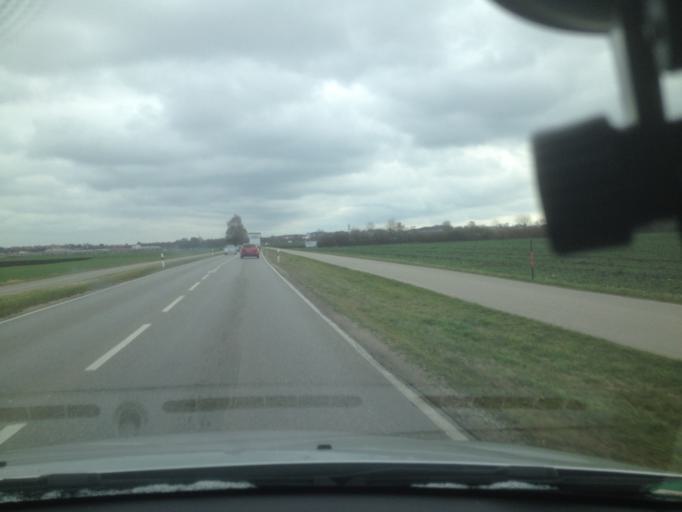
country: DE
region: Bavaria
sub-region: Swabia
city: Mering
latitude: 48.2686
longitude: 10.9585
